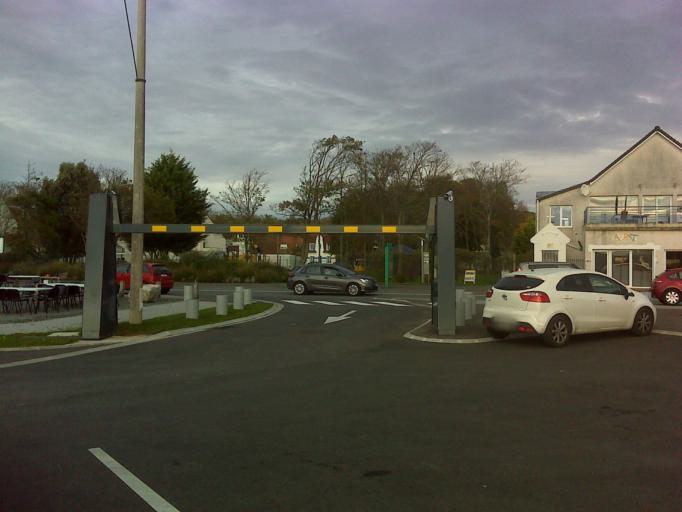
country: FR
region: Nord-Pas-de-Calais
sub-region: Departement du Pas-de-Calais
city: Etaples
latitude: 50.5187
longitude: 1.6293
